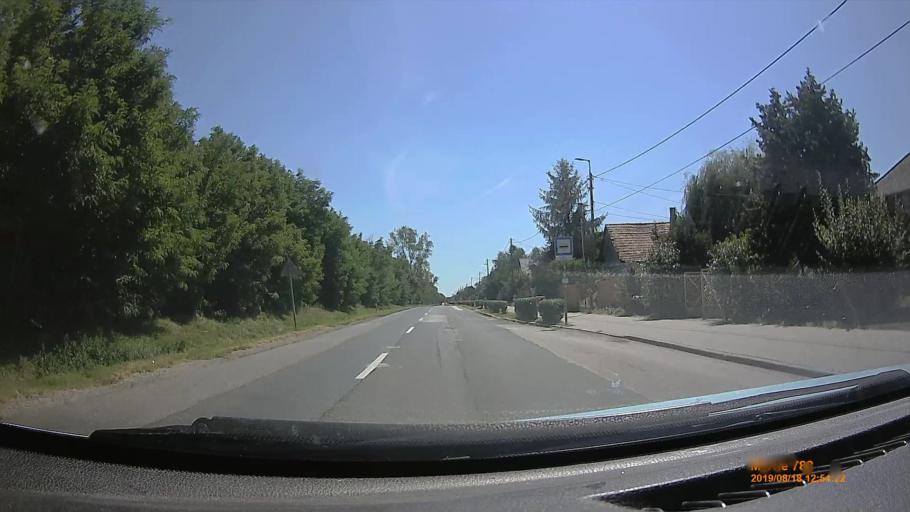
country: HU
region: Fejer
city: Aba
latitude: 47.0421
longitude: 18.5311
